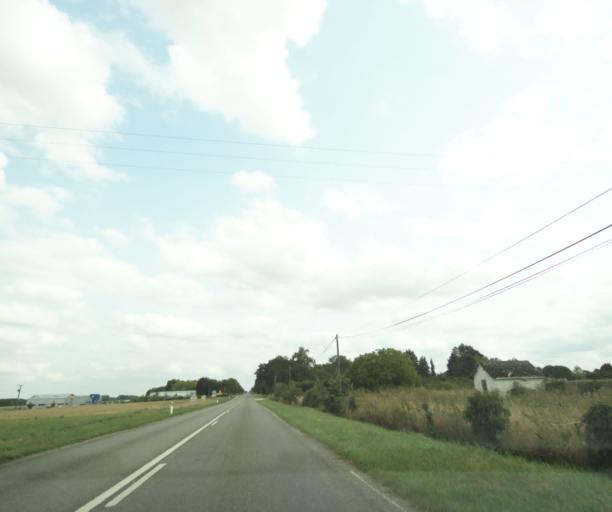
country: FR
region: Centre
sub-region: Departement de l'Indre
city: Buzancais
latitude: 46.8873
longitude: 1.4358
